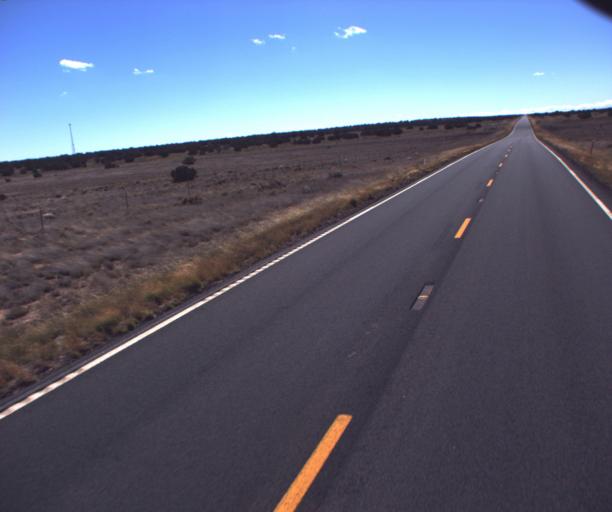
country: US
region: Arizona
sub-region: Apache County
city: Houck
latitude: 34.9200
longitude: -109.2383
